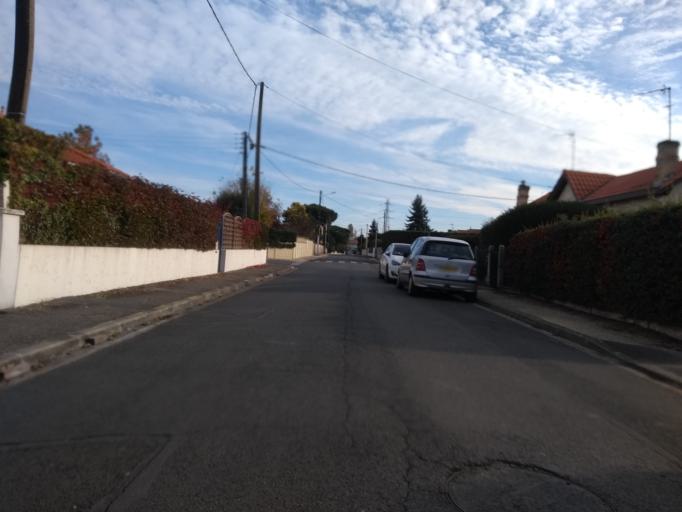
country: FR
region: Aquitaine
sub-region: Departement de la Gironde
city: Pessac
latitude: 44.7921
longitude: -0.6706
